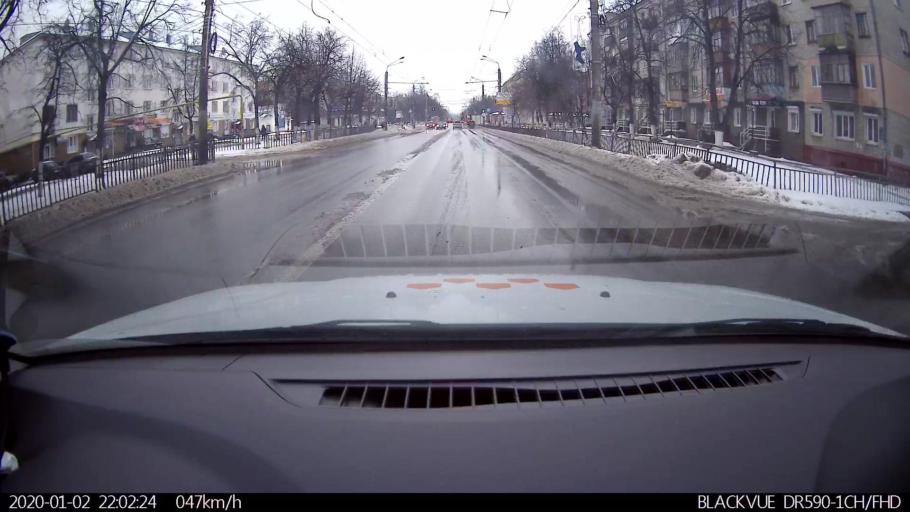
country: RU
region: Nizjnij Novgorod
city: Gorbatovka
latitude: 56.2473
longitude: 43.8650
